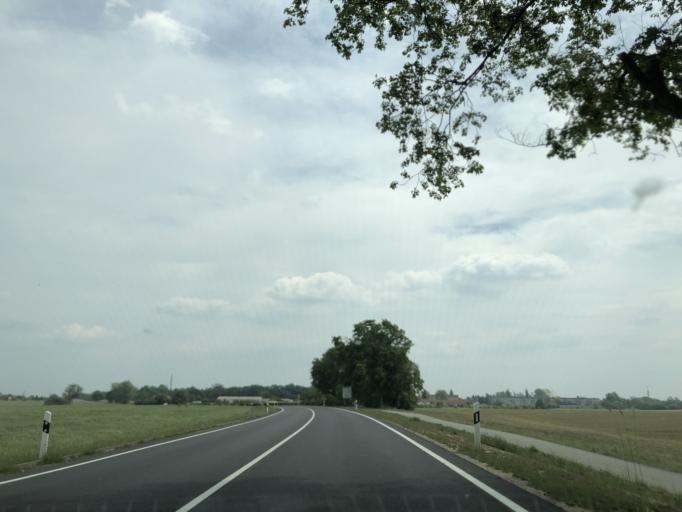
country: DE
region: Brandenburg
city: Kyritz
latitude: 52.9539
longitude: 12.3699
